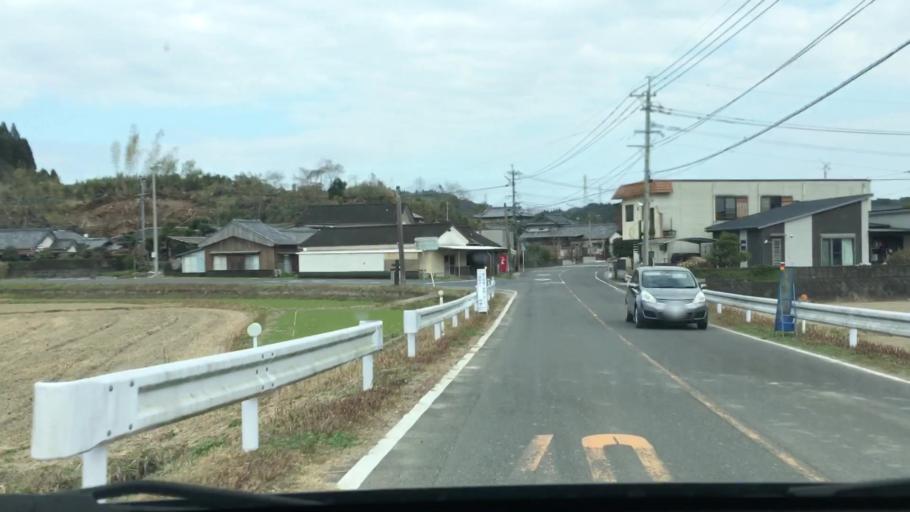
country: JP
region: Miyazaki
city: Kushima
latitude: 31.4674
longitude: 131.2087
